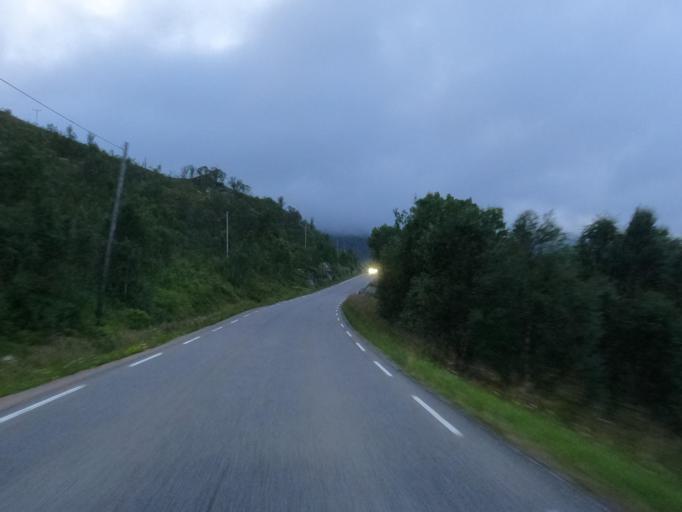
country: NO
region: Nordland
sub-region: Lodingen
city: Lodingen
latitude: 68.6078
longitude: 15.7777
